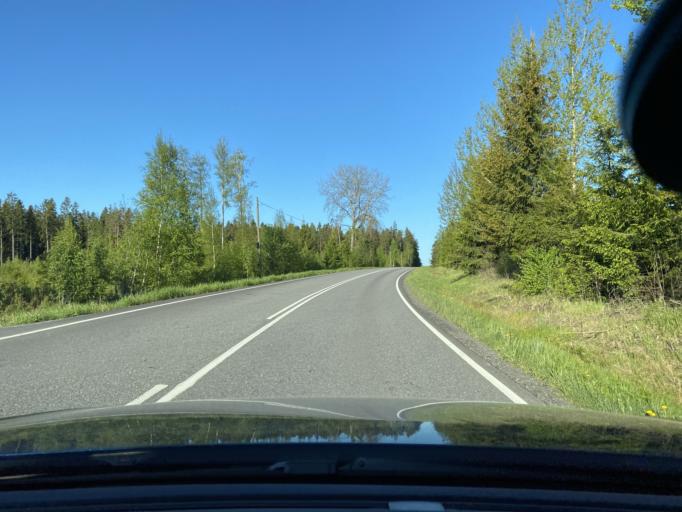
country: FI
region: Varsinais-Suomi
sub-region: Loimaa
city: Alastaro
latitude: 60.8765
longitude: 22.7867
